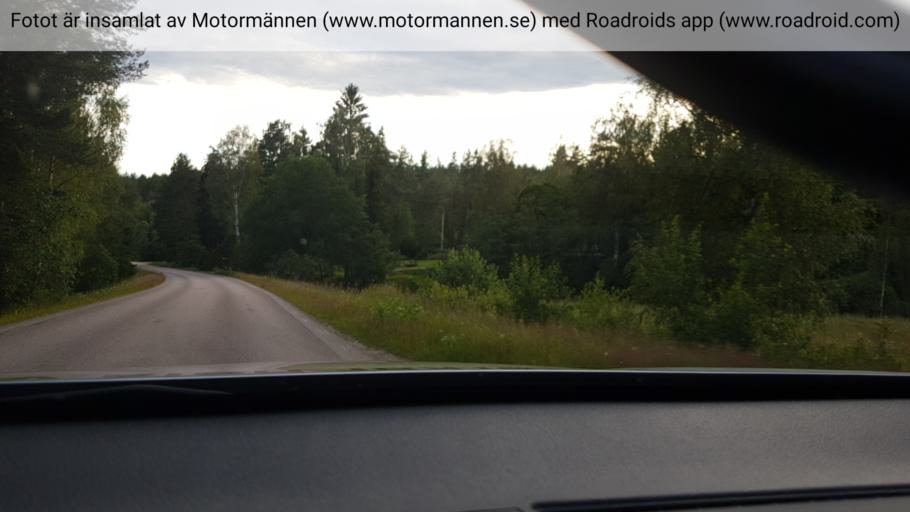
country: SE
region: Vaermland
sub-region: Forshaga Kommun
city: Deje
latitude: 59.7468
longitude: 13.3758
